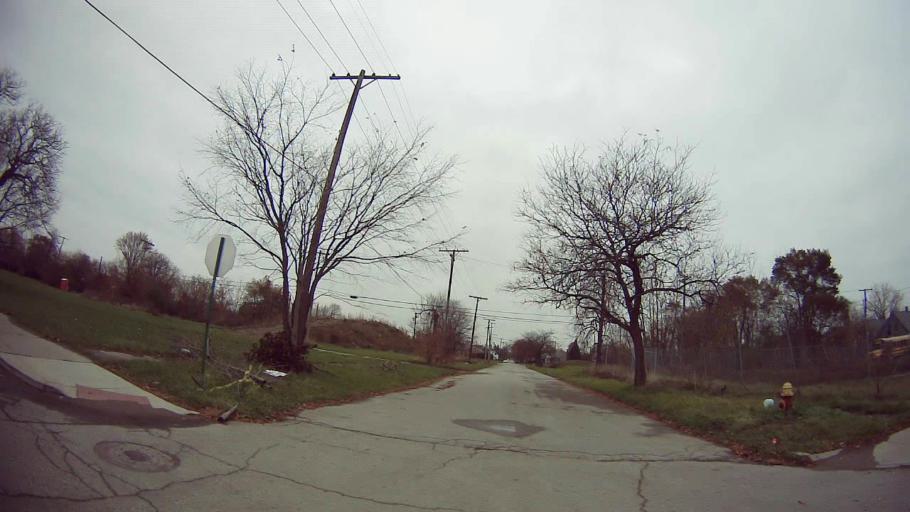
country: US
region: Michigan
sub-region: Wayne County
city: Hamtramck
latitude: 42.3658
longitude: -83.0452
